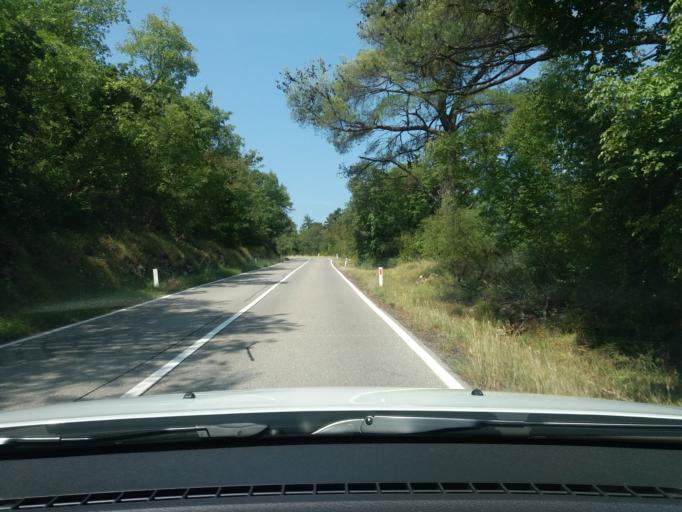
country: SI
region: Miren-Kostanjevica
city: Miren
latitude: 45.8809
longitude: 13.6019
